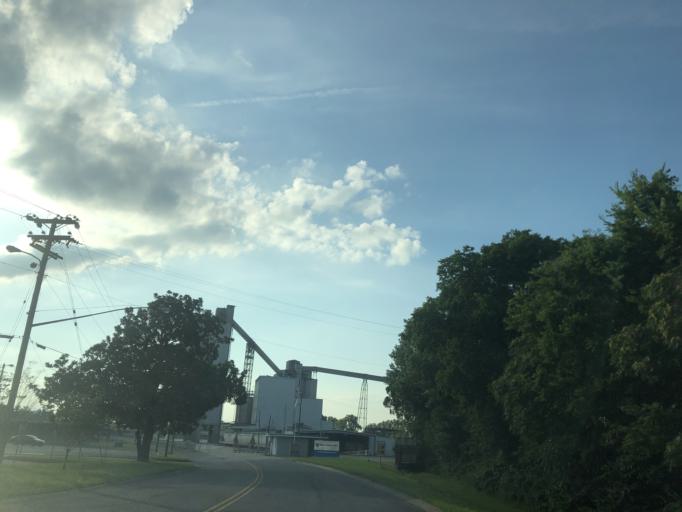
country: US
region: Tennessee
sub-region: Davidson County
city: Nashville
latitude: 36.1861
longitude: -86.7867
